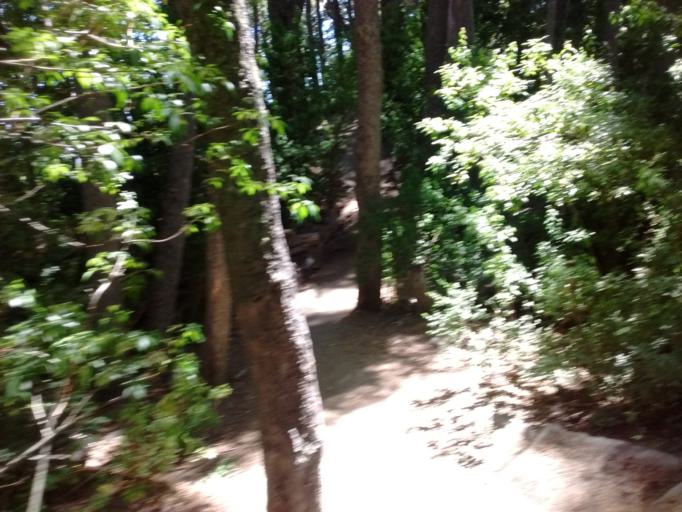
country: AR
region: Neuquen
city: Villa La Angostura
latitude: -40.7876
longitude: -71.6597
